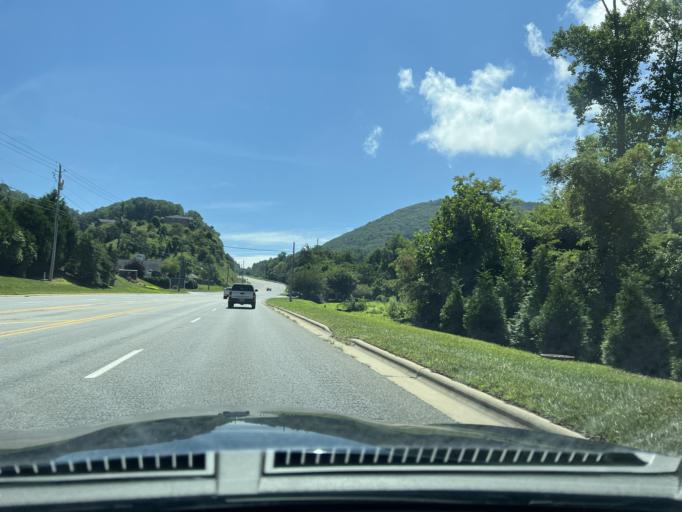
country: US
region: North Carolina
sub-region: Buncombe County
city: Biltmore Forest
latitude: 35.5494
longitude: -82.4666
